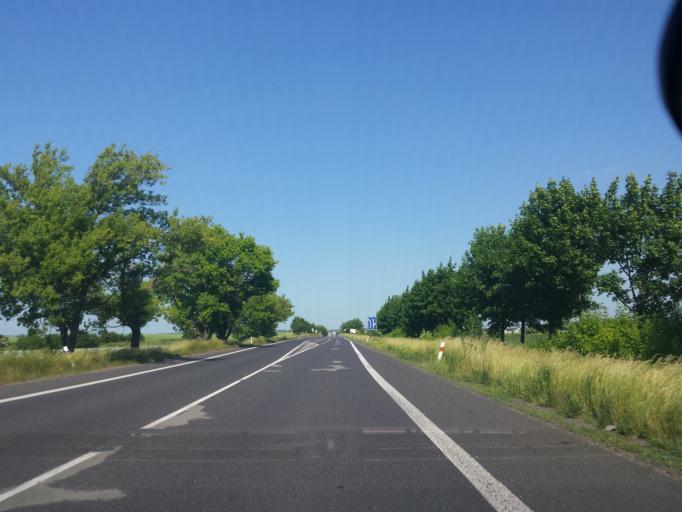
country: CZ
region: Central Bohemia
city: Luzec nad Vltavou
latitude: 50.3394
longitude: 14.3848
